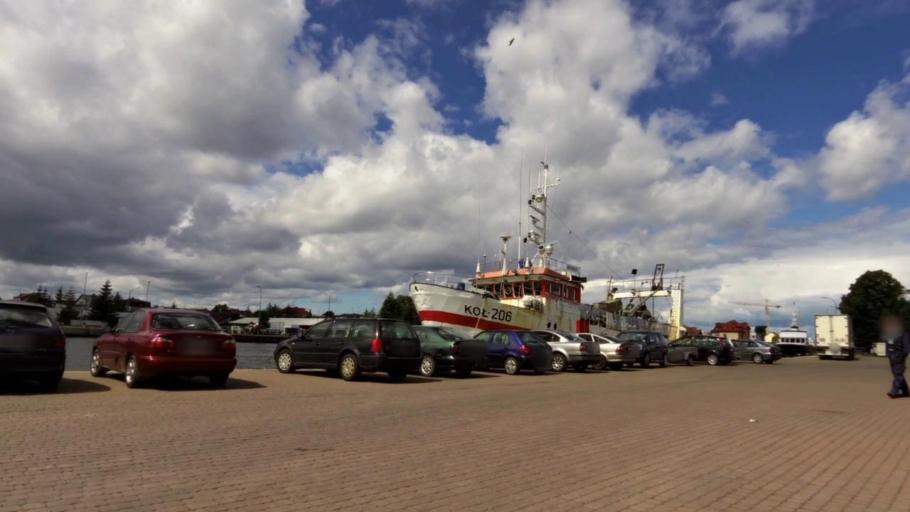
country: PL
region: West Pomeranian Voivodeship
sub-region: Powiat slawienski
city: Darlowo
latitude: 54.4380
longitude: 16.3845
